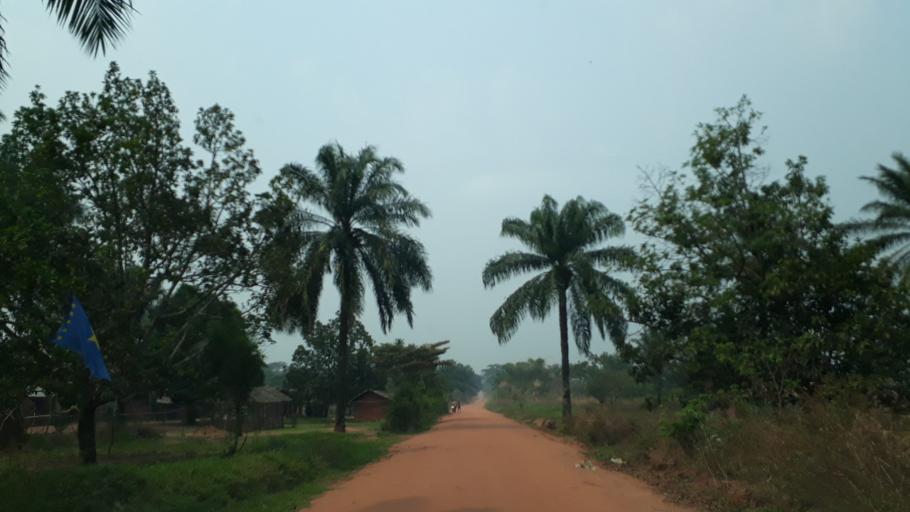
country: CD
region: Kasai-Occidental
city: Tshikapa
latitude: -6.4866
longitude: 20.4216
